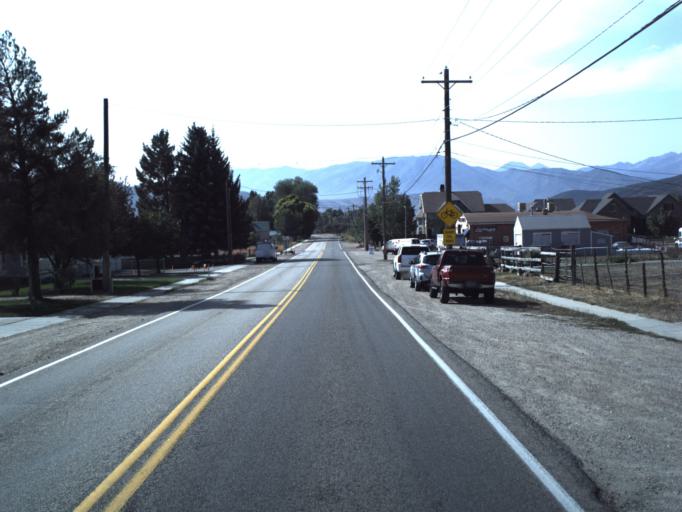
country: US
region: Utah
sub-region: Wasatch County
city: Midway
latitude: 40.5087
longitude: -111.4724
